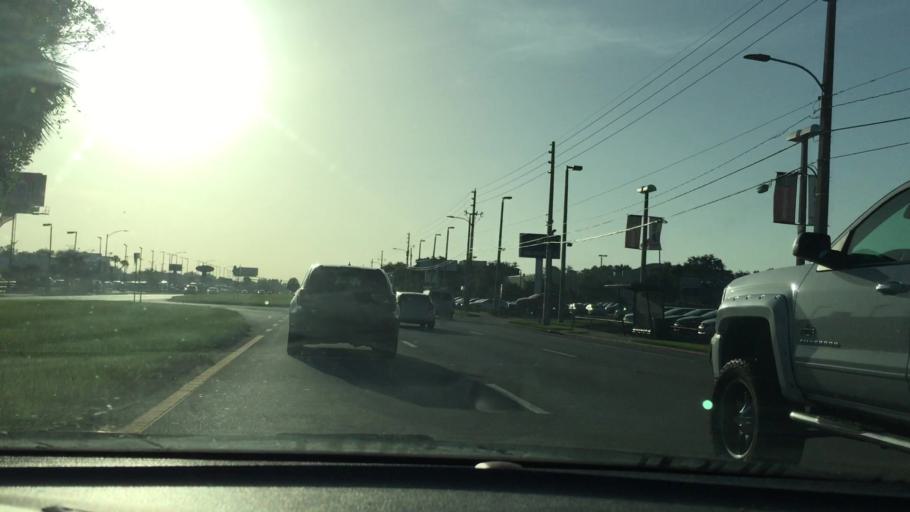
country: US
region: Florida
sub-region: Orange County
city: Pine Hills
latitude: 28.5526
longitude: -81.4244
